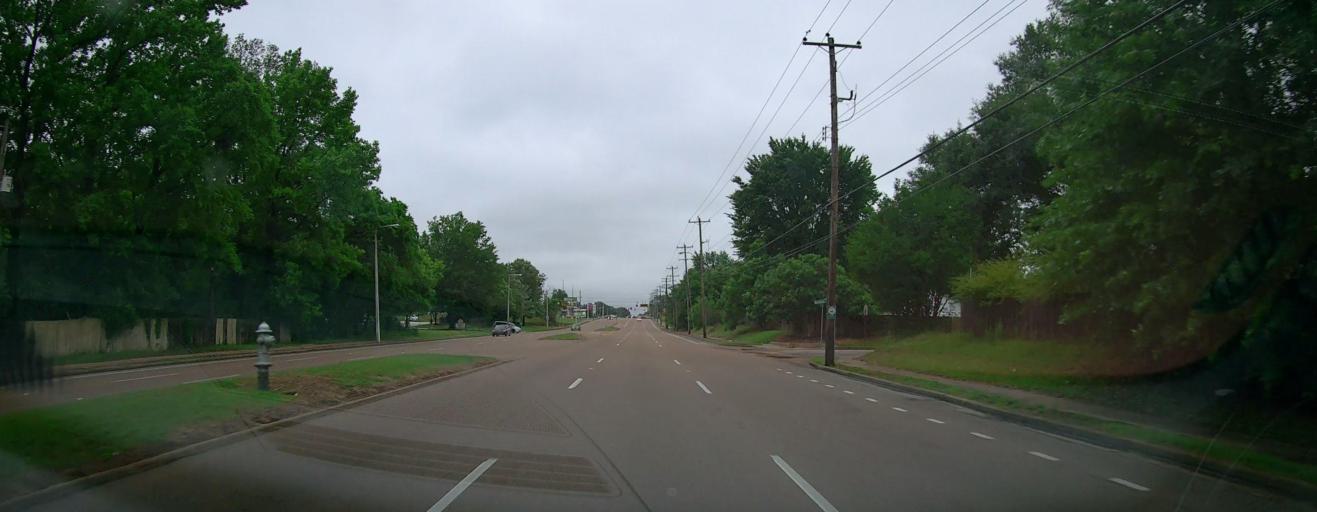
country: US
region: Mississippi
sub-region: De Soto County
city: Olive Branch
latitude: 35.0251
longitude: -89.8314
